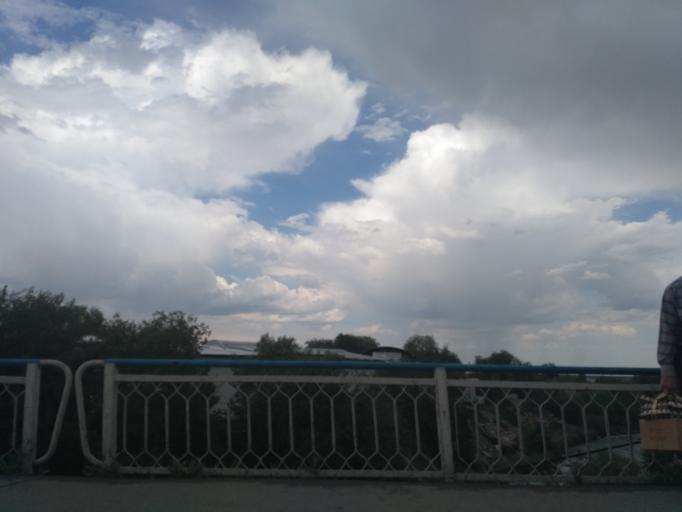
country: KZ
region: Almaty Oblysy
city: Burunday
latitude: 43.2010
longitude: 76.6294
